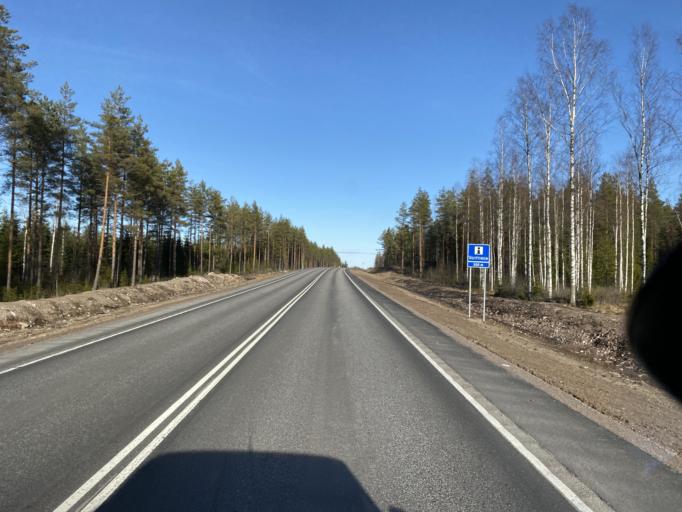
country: FI
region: Satakunta
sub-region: Pori
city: Kokemaeki
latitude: 61.1702
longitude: 22.4698
